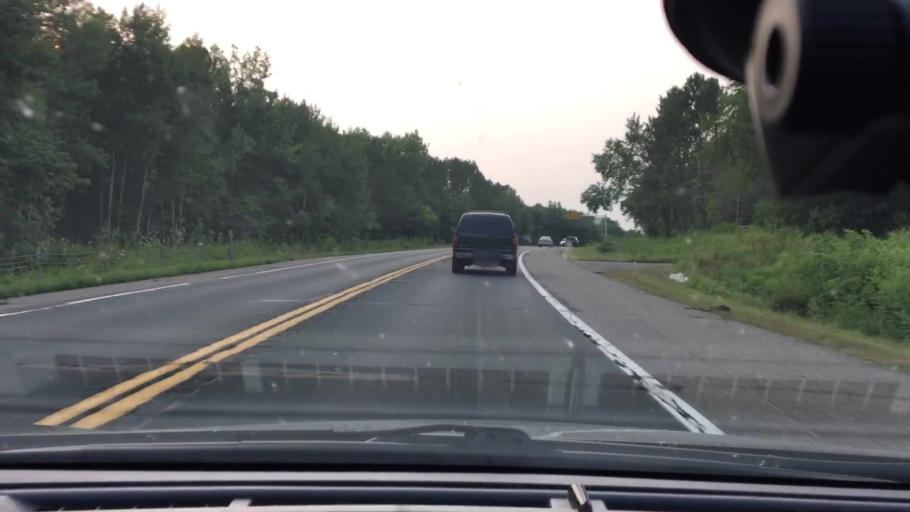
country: US
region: Minnesota
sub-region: Mille Lacs County
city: Vineland
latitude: 46.2036
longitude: -93.7818
